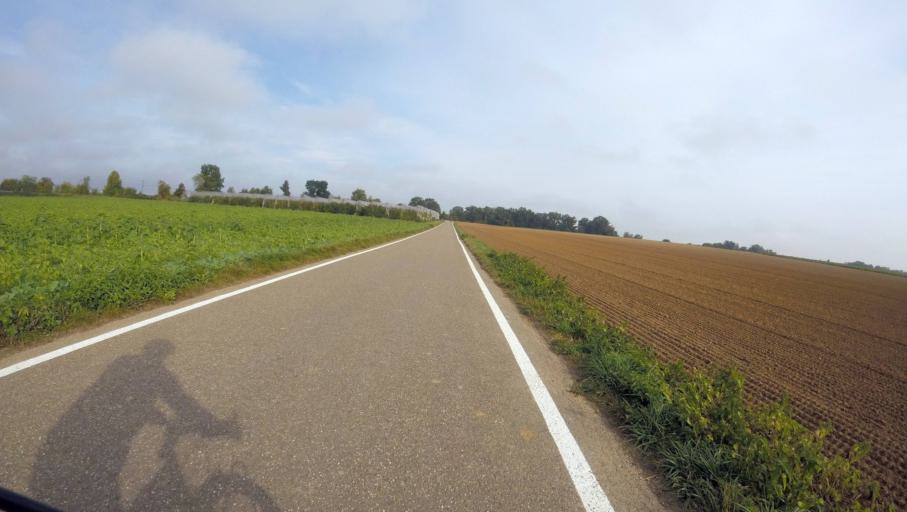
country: DE
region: Baden-Wuerttemberg
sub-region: Regierungsbezirk Stuttgart
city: Bondorf
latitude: 48.5294
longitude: 8.8288
